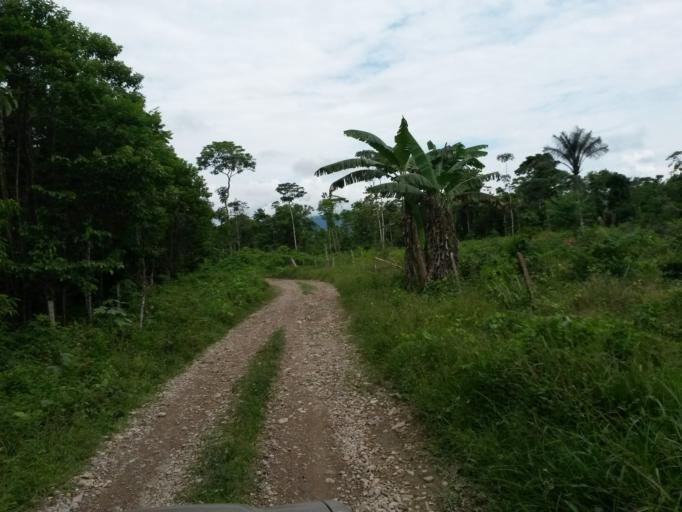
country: CO
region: Putumayo
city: Puerto Guzman
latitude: 1.0240
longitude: -76.3759
